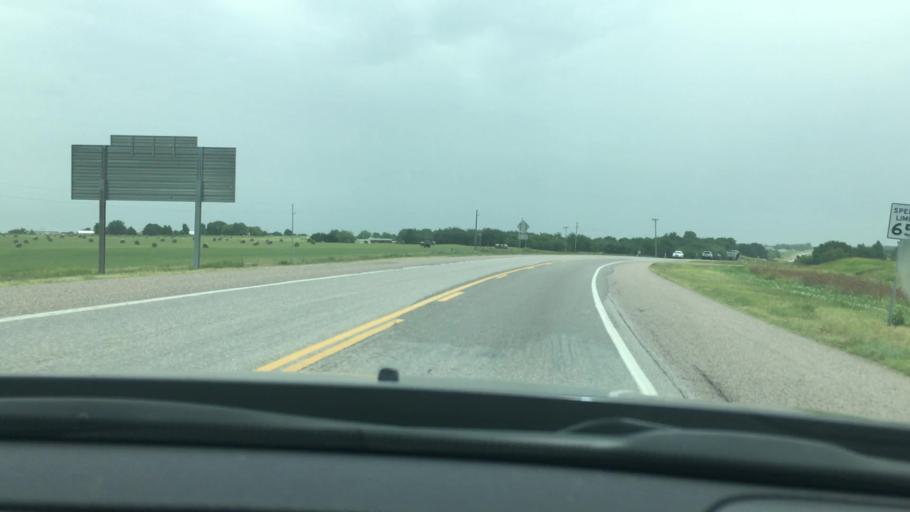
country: US
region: Oklahoma
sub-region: Pontotoc County
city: Ada
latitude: 34.6590
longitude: -96.7946
